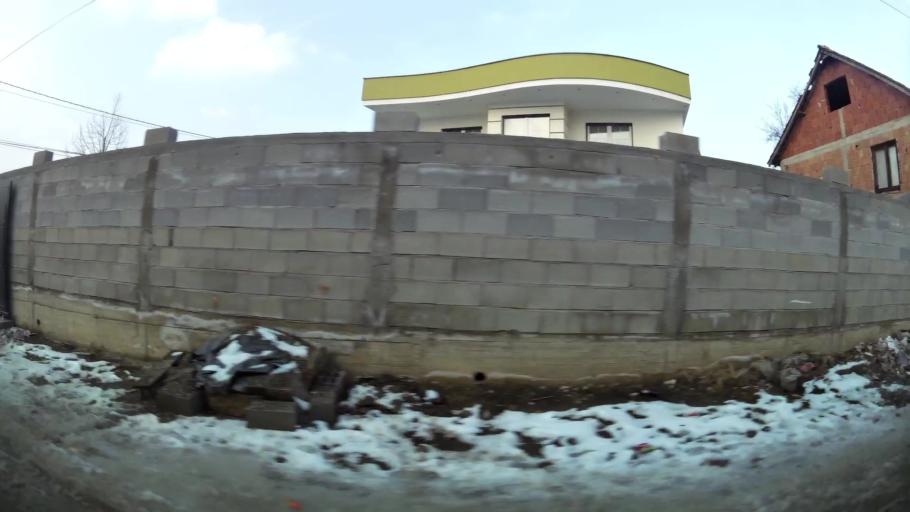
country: MK
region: Aracinovo
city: Arachinovo
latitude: 42.0233
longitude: 21.5611
